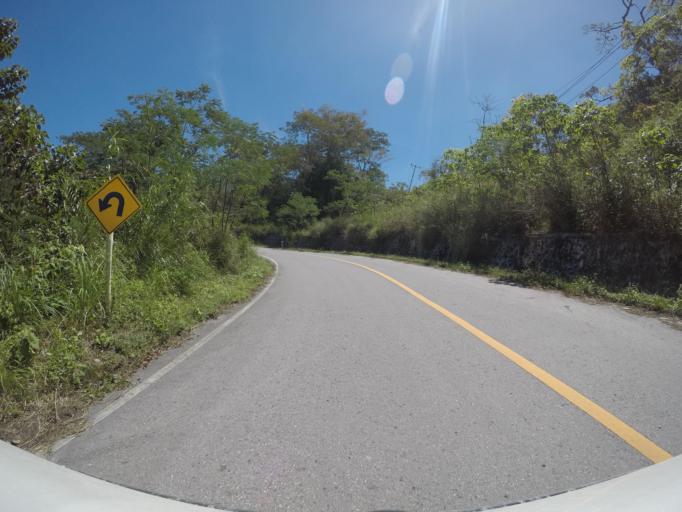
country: TL
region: Manatuto
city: Manatuto
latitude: -8.7710
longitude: 125.9648
